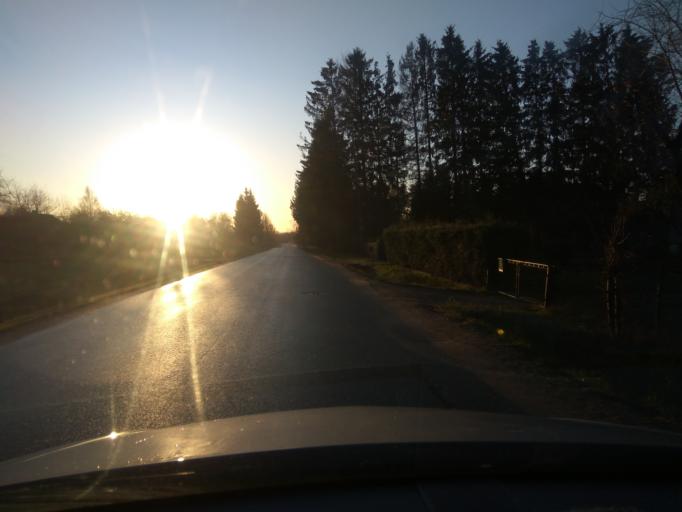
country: LV
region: Kuldigas Rajons
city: Kuldiga
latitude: 56.9714
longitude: 21.9970
